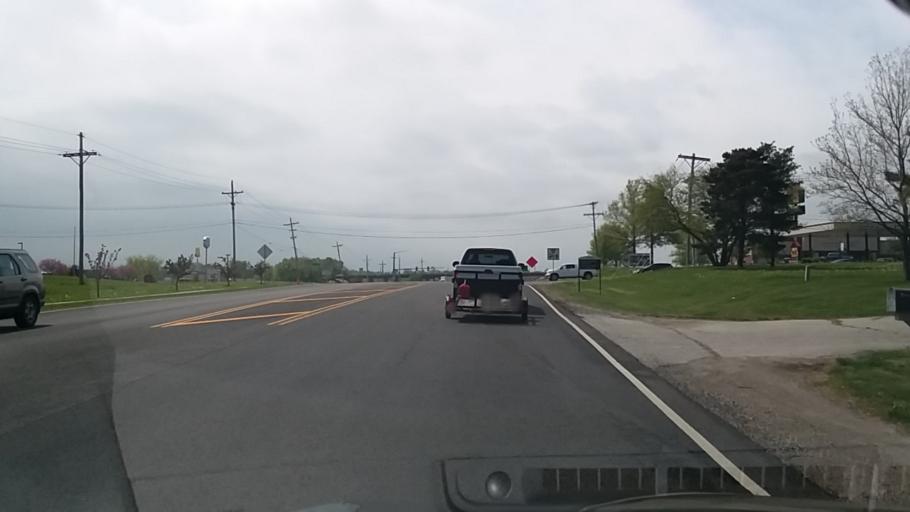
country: US
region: Kansas
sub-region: Johnson County
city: De Soto
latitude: 38.9648
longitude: -94.9832
